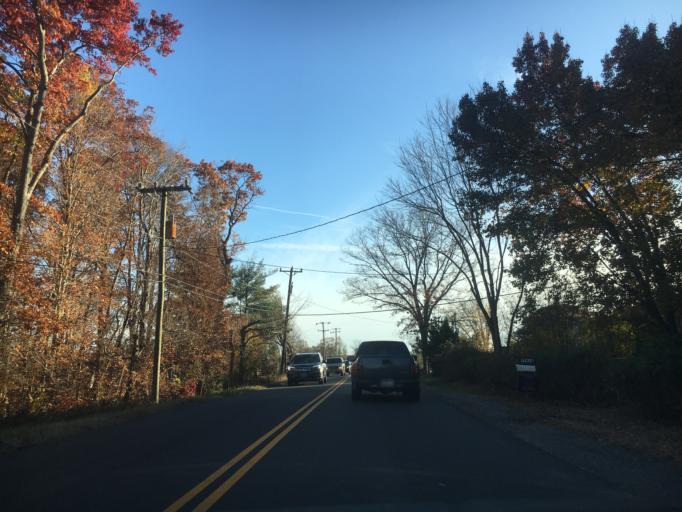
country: US
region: Virginia
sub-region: Prince William County
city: Dumfries
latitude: 38.5755
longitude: -77.3302
